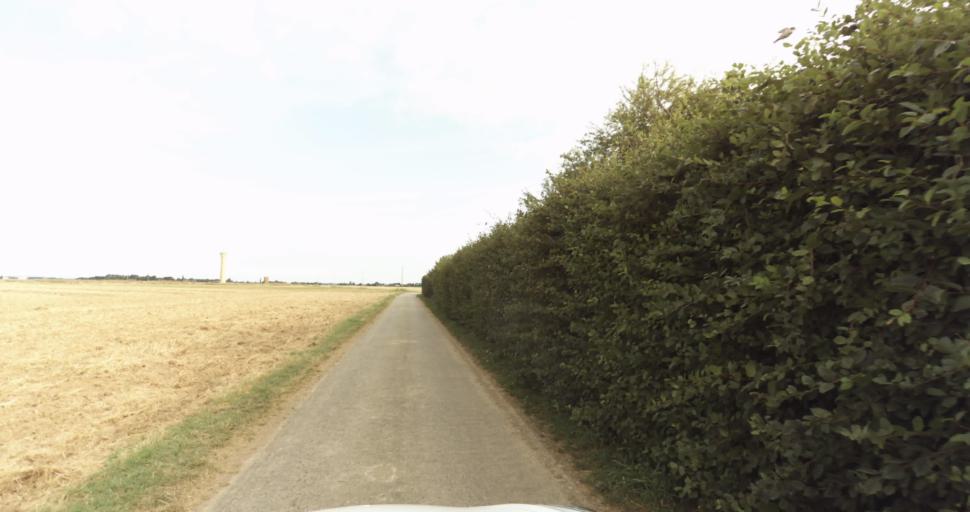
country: FR
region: Haute-Normandie
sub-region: Departement de l'Eure
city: La Madeleine-de-Nonancourt
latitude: 48.8672
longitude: 1.2435
